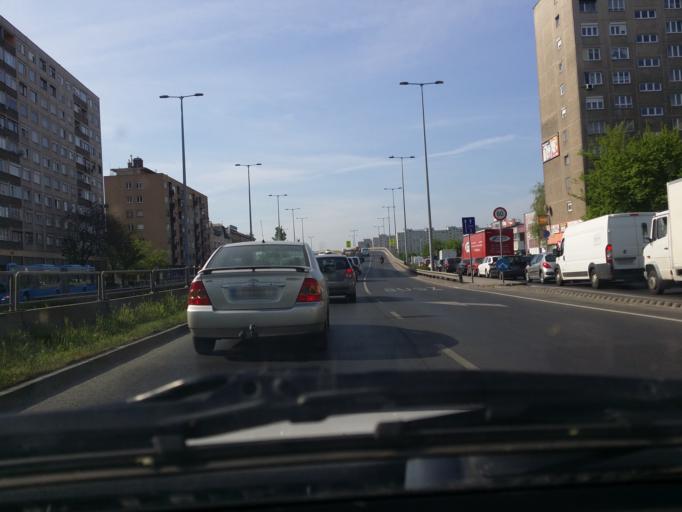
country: HU
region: Budapest
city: Budapest III. keruelet
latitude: 47.5435
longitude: 19.0421
